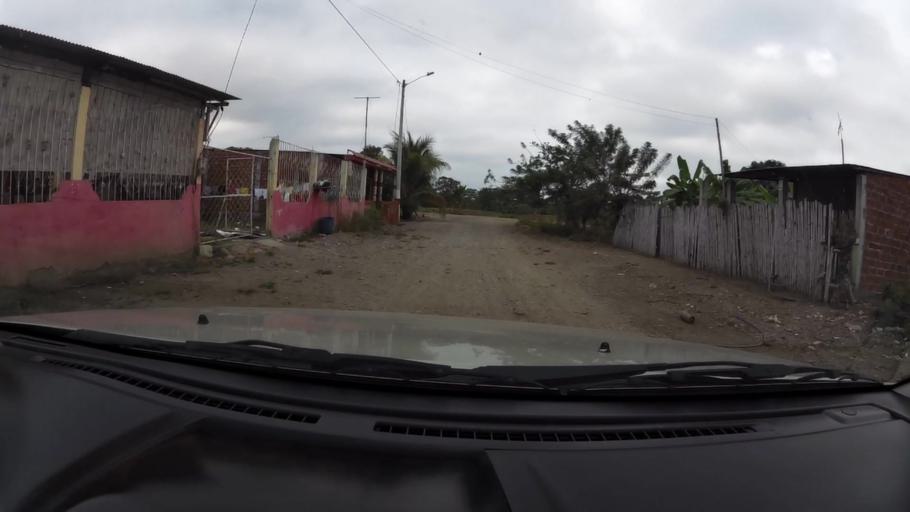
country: EC
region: Guayas
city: Yaguachi Nuevo
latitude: -2.2442
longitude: -79.6430
